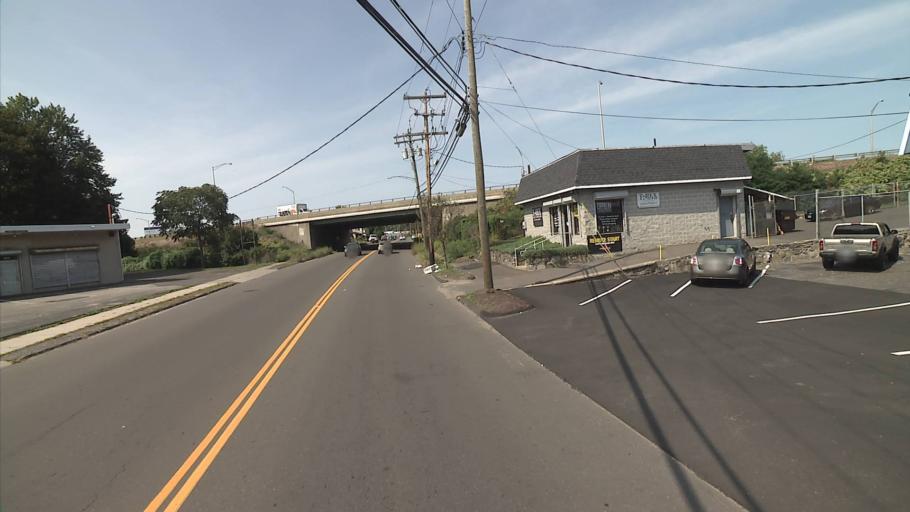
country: US
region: Connecticut
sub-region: Fairfield County
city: Stratford
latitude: 41.1869
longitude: -73.1358
